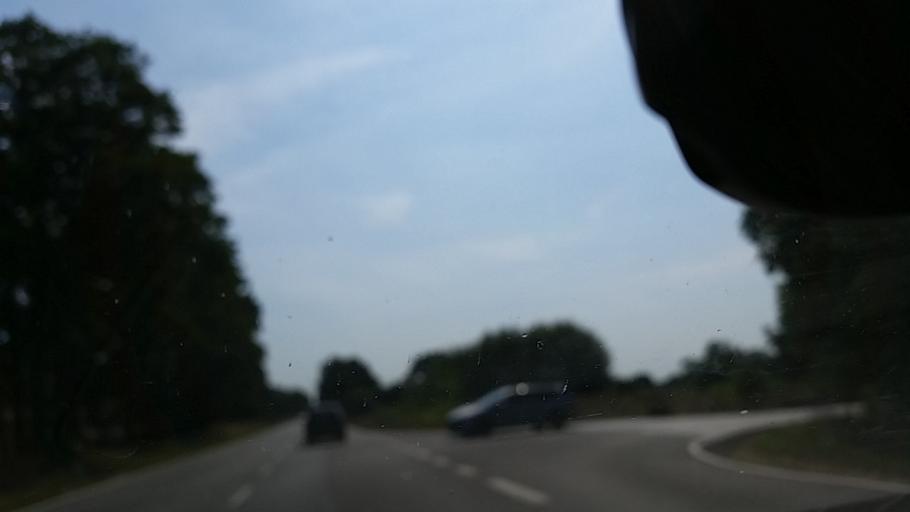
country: DE
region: Lower Saxony
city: Diepholz
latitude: 52.6073
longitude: 8.3351
